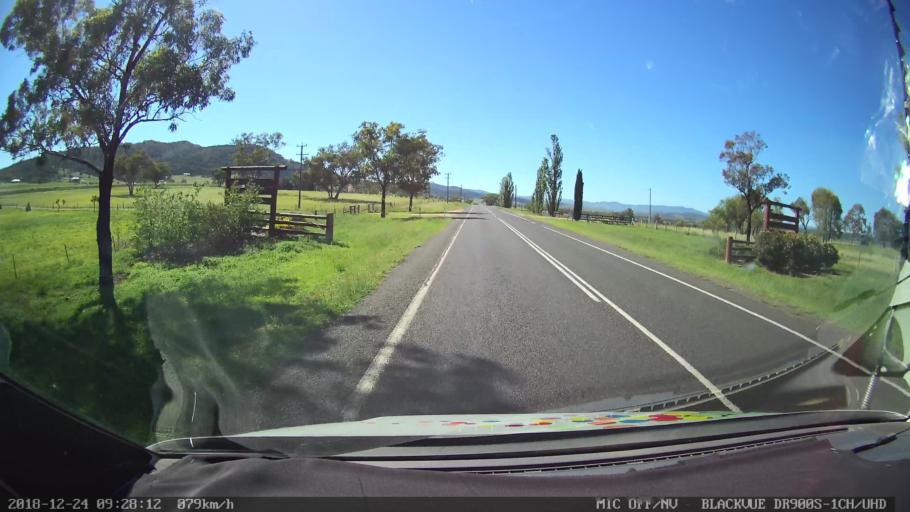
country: AU
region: New South Wales
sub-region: Liverpool Plains
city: Quirindi
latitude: -31.5353
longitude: 150.6868
